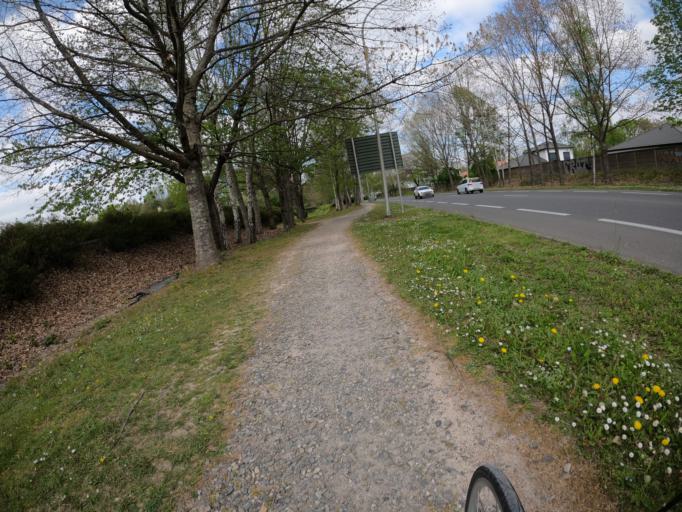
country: FR
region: Aquitaine
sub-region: Departement des Pyrenees-Atlantiques
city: Lons
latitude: 43.3322
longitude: -0.3847
